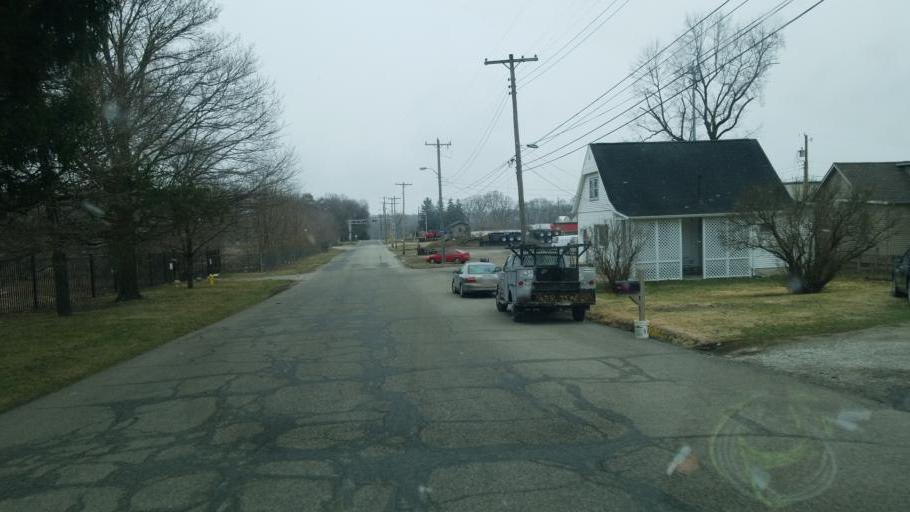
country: US
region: Indiana
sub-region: Wabash County
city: Wabash
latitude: 40.8024
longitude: -85.8425
